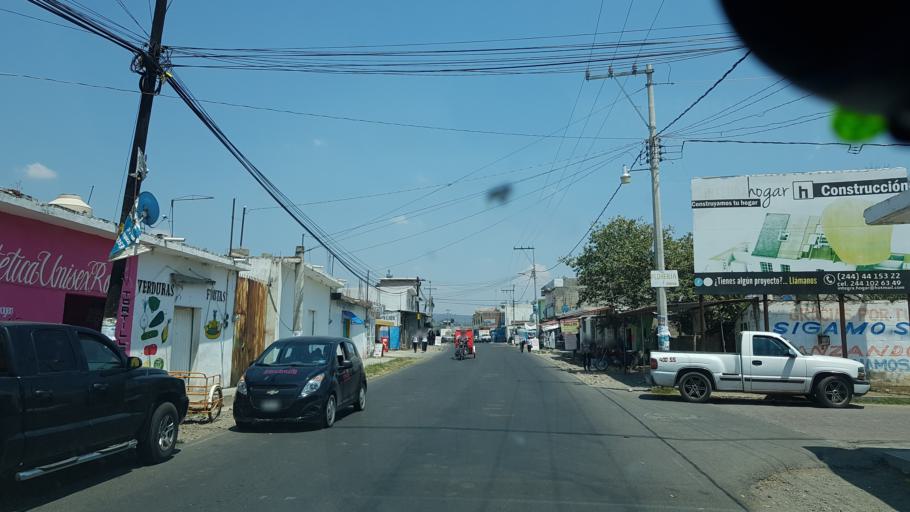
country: MX
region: Puebla
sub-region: Huaquechula
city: Cacaloxuchitl
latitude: 18.7866
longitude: -98.4850
